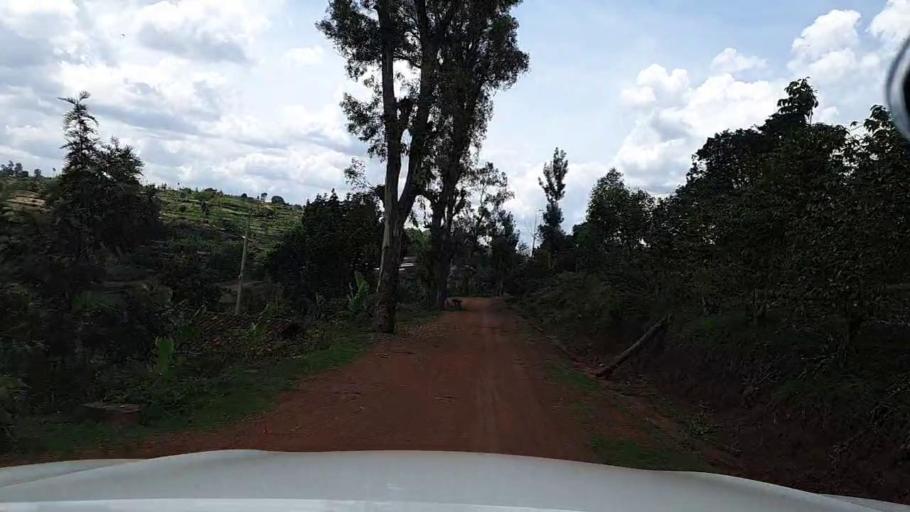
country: RW
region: Southern Province
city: Butare
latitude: -2.7601
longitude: 29.7465
